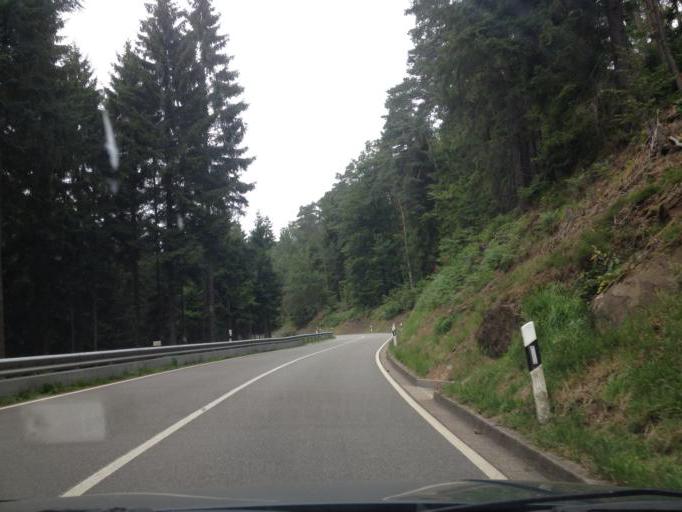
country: DE
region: Rheinland-Pfalz
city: Elmstein
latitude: 49.3084
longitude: 7.8677
